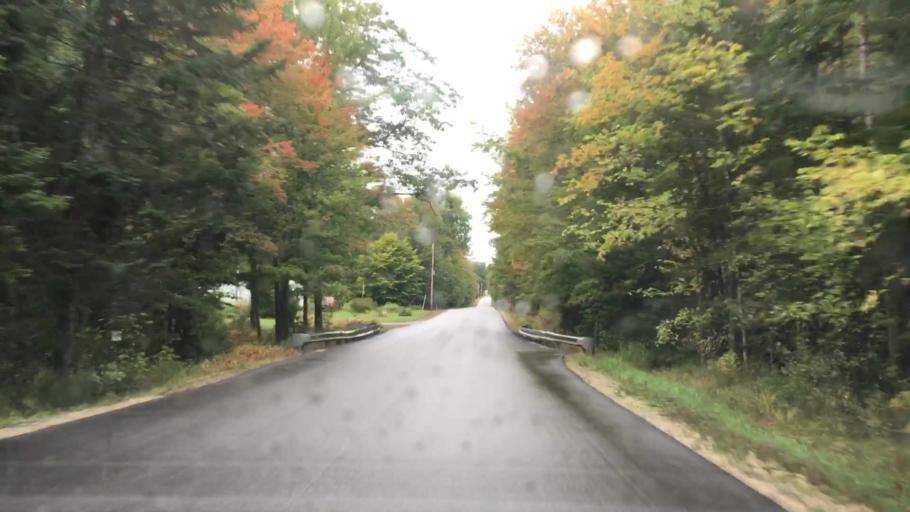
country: US
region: Maine
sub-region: Cumberland County
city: Harrison
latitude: 44.0821
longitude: -70.6452
